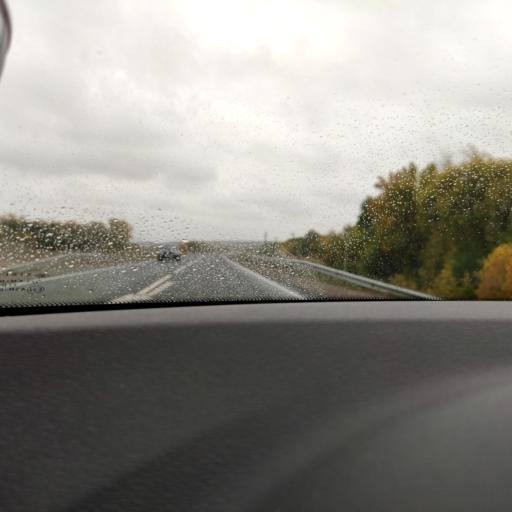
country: RU
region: Samara
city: Mirnyy
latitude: 53.6287
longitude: 50.2469
